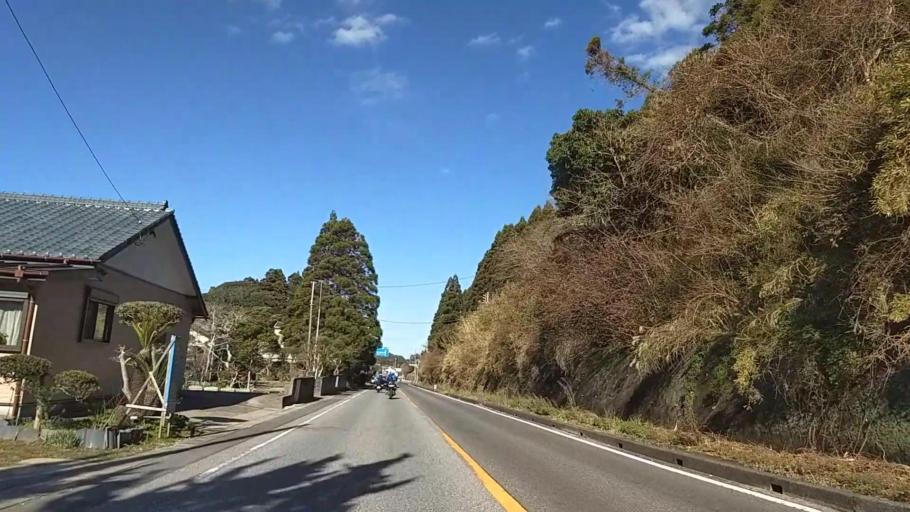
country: JP
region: Chiba
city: Ohara
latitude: 35.2087
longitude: 140.3750
